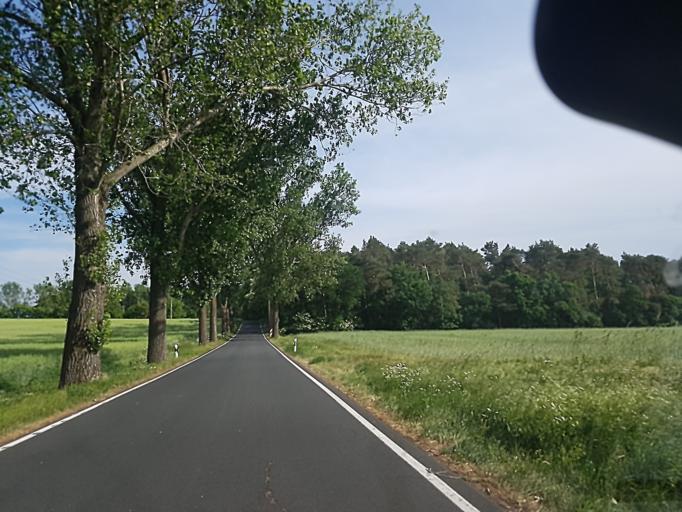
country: DE
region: Saxony-Anhalt
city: Kropstadt
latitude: 51.9707
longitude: 12.7358
